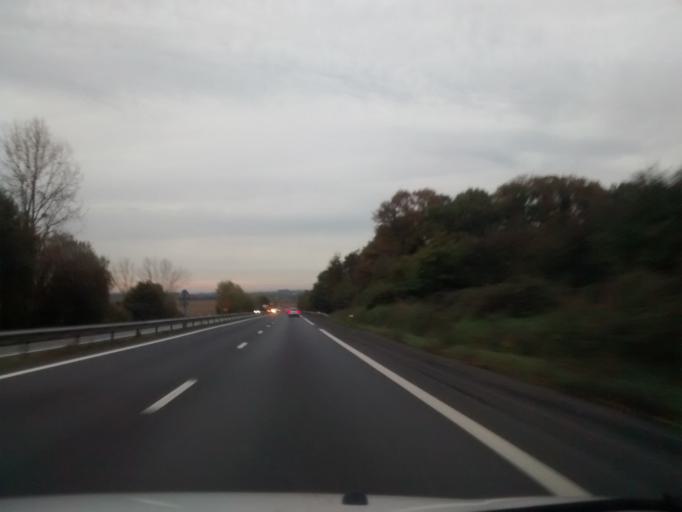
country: FR
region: Brittany
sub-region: Departement des Cotes-d'Armor
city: Plumaugat
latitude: 48.2873
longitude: -2.2044
